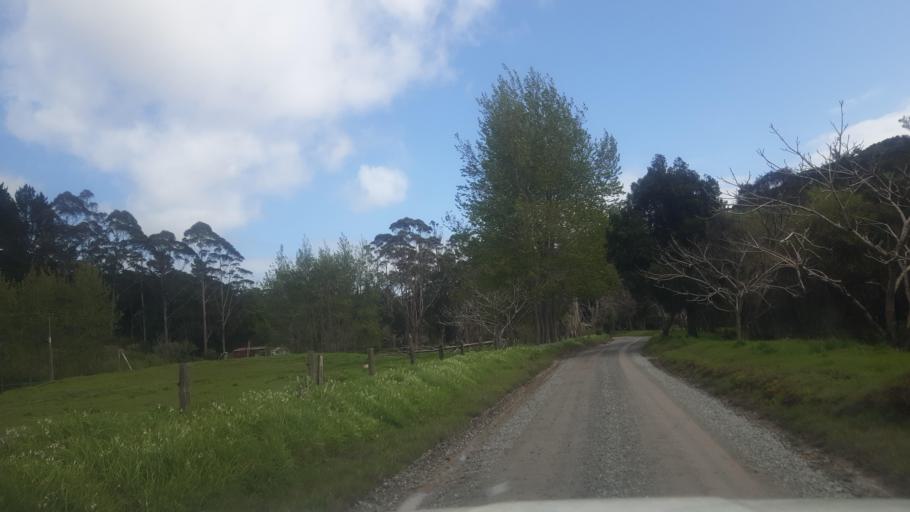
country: NZ
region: Northland
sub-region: Far North District
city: Taipa
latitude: -35.1139
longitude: 173.4309
